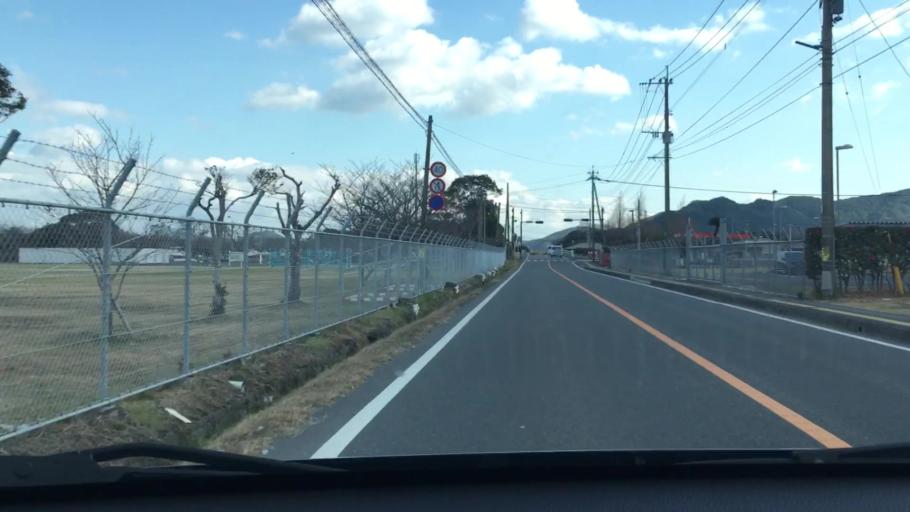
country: JP
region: Oita
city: Saiki
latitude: 32.9695
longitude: 131.9136
